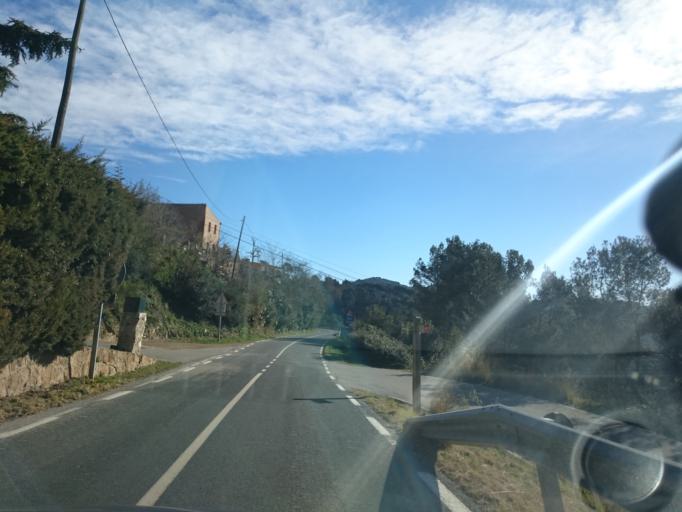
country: ES
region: Catalonia
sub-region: Provincia de Barcelona
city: Sant Just Desvern
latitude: 41.4083
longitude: 2.0887
